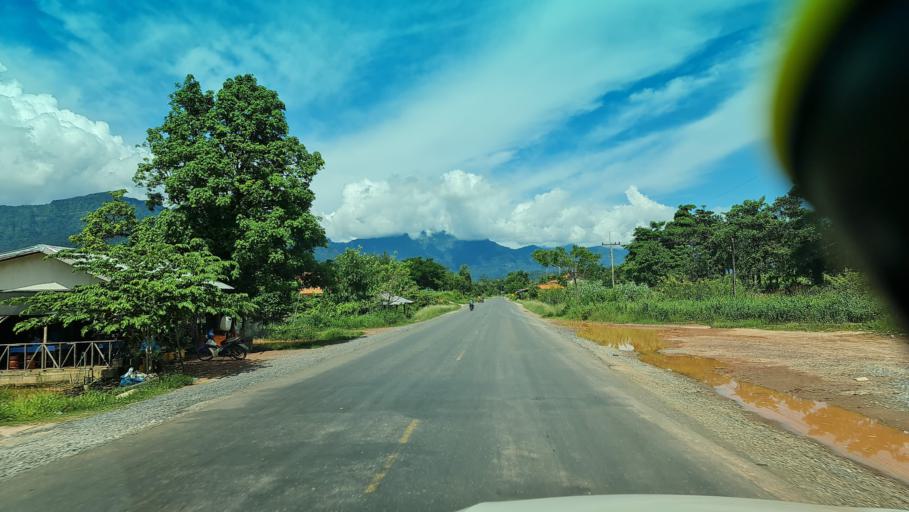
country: LA
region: Bolikhamxai
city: Ban Nahin
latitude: 18.3003
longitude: 104.1217
